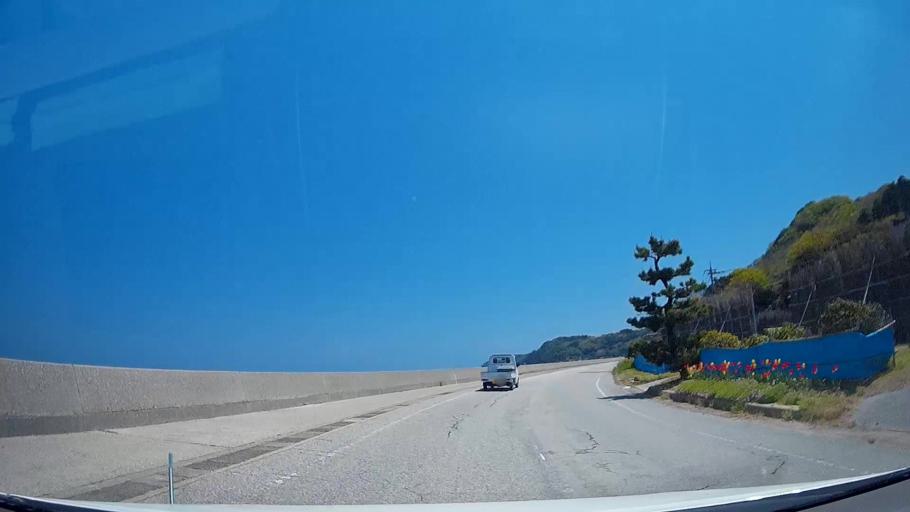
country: JP
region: Ishikawa
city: Nanao
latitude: 37.5297
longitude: 137.2891
